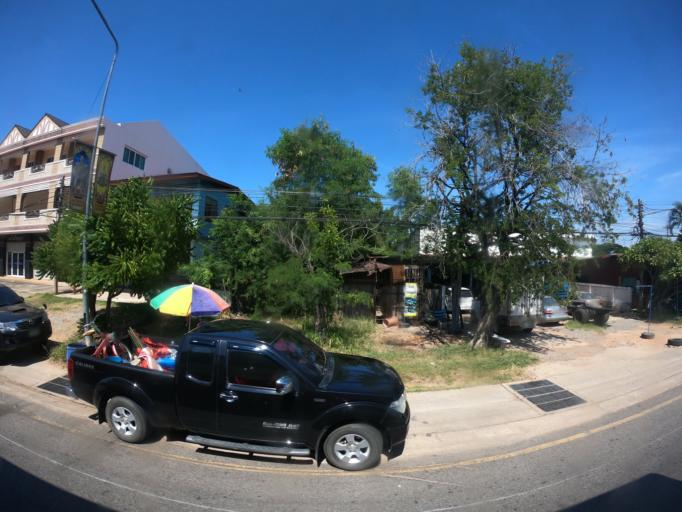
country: TH
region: Khon Kaen
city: Ban Phai
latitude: 16.0575
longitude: 102.7175
